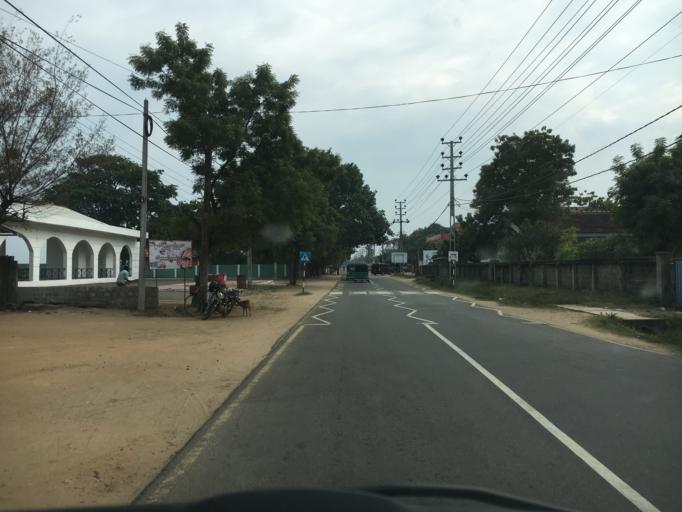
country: LK
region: Eastern Province
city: Trincomalee
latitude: 8.5013
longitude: 81.1918
